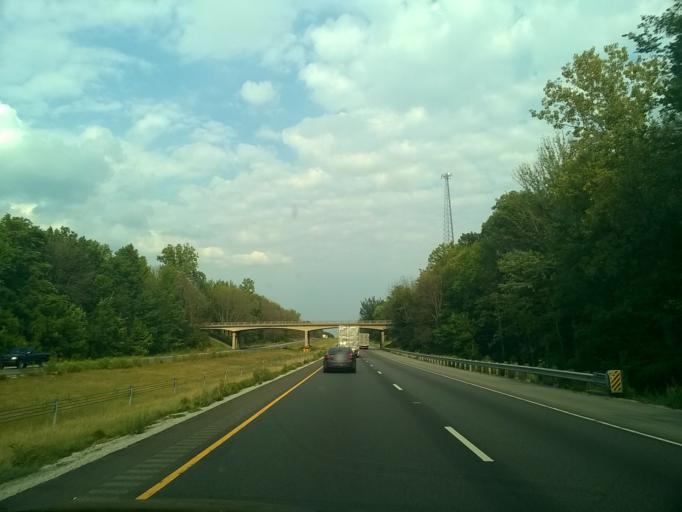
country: US
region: Indiana
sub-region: Clay County
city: Brazil
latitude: 39.4662
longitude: -87.0533
